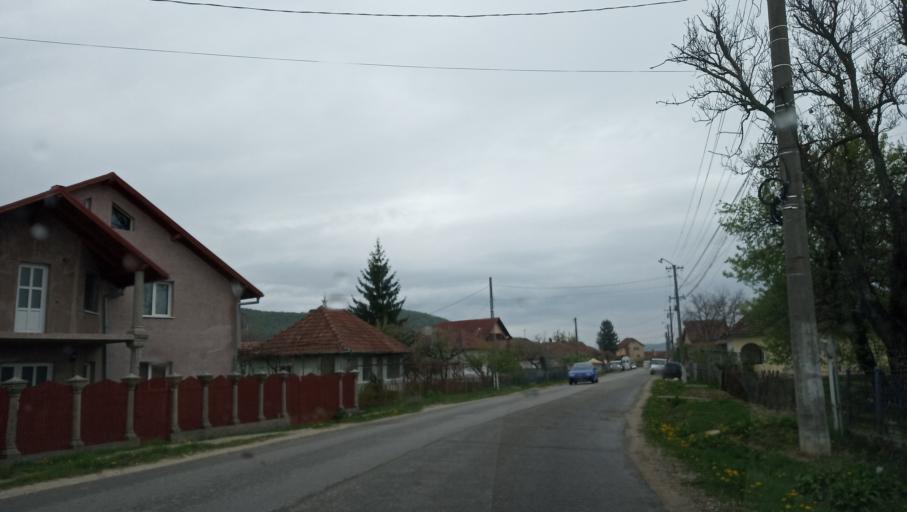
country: RO
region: Valcea
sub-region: Oras Calimanesti
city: Jiblea Veche
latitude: 45.2407
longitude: 24.3617
